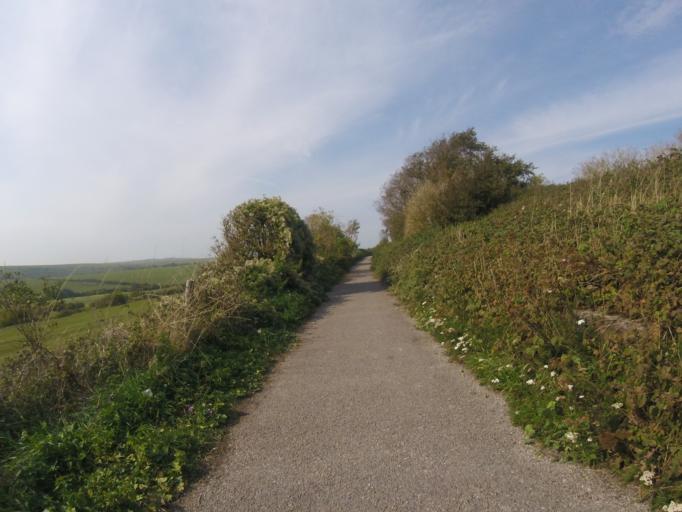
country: GB
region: England
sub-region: East Sussex
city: Portslade
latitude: 50.8597
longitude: -0.2014
